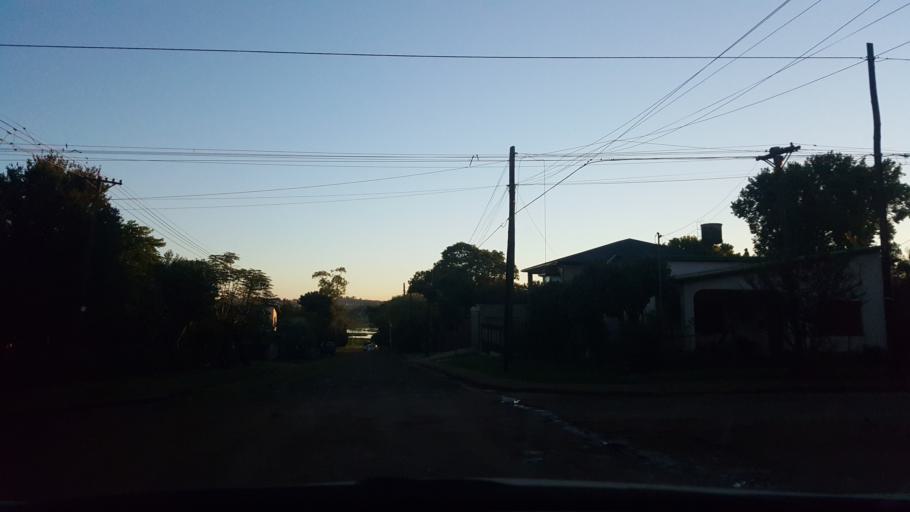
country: AR
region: Misiones
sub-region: Departamento de Capital
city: Posadas
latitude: -27.4254
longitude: -55.9007
